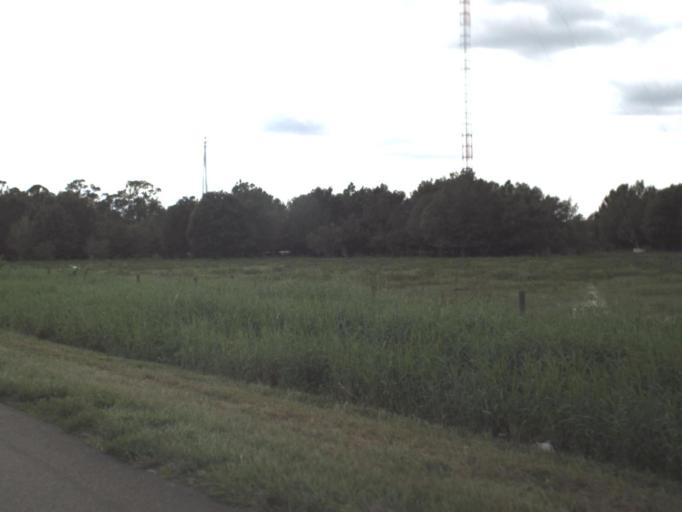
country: US
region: Florida
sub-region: Lee County
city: Fort Myers Shores
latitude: 26.8169
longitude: -81.7602
